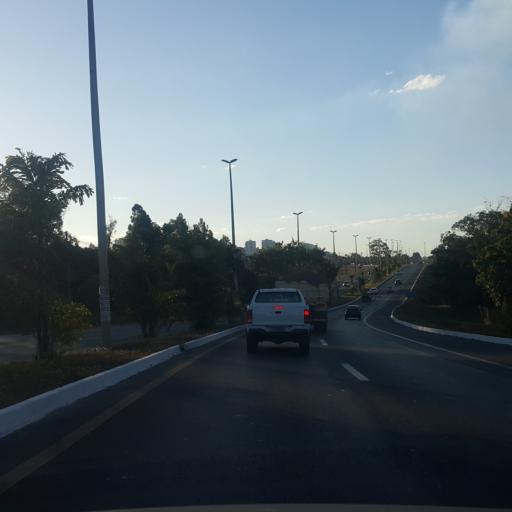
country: BR
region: Federal District
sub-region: Brasilia
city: Brasilia
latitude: -15.8486
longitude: -47.9986
